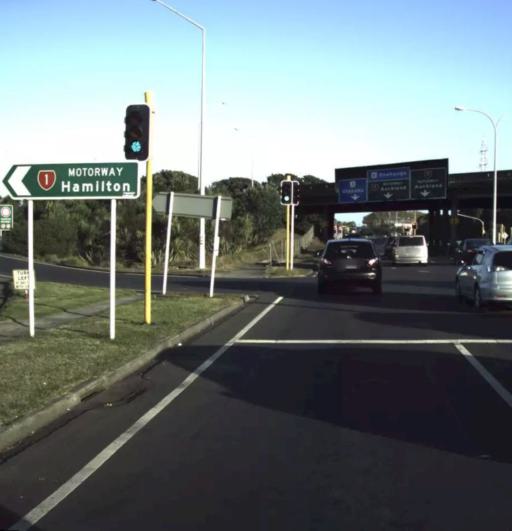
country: NZ
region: Auckland
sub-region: Auckland
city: Tamaki
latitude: -36.9181
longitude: 174.8399
